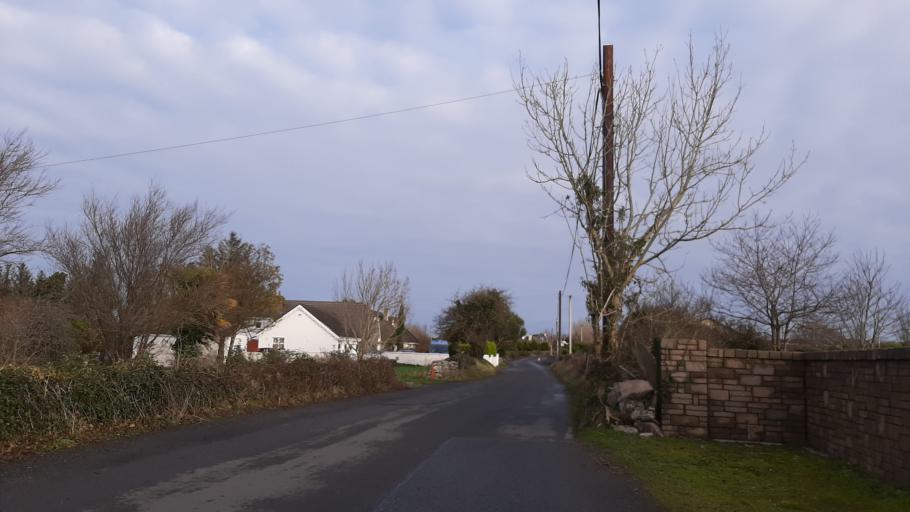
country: IE
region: Connaught
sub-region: County Galway
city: Gaillimh
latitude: 53.3071
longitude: -9.0594
